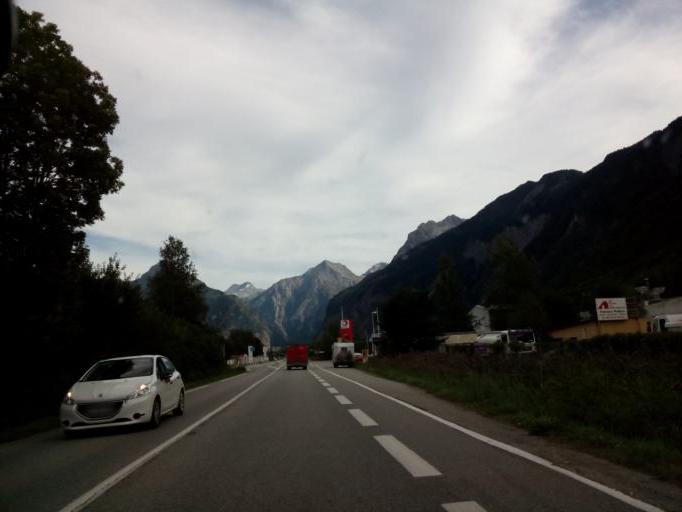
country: FR
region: Rhone-Alpes
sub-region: Departement de l'Isere
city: Huez
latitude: 45.0680
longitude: 6.0211
